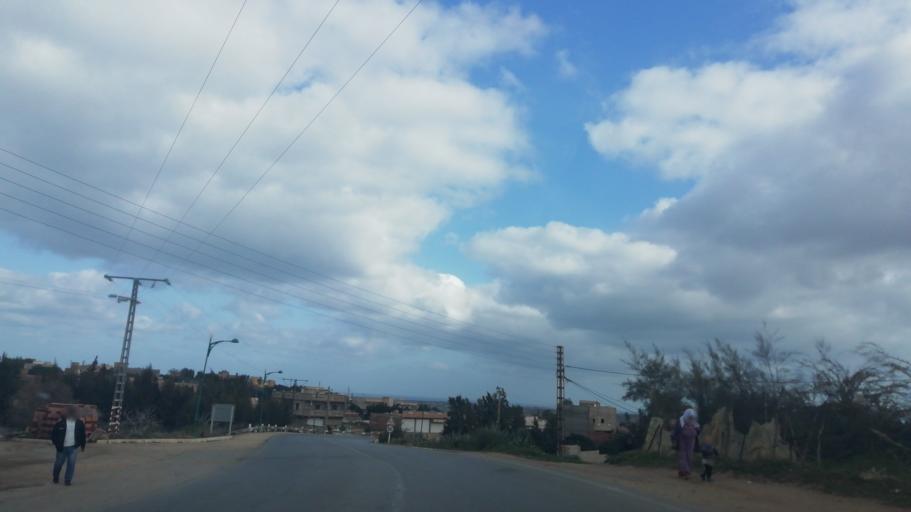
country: DZ
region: Relizane
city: Mazouna
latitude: 36.2837
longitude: 0.6442
